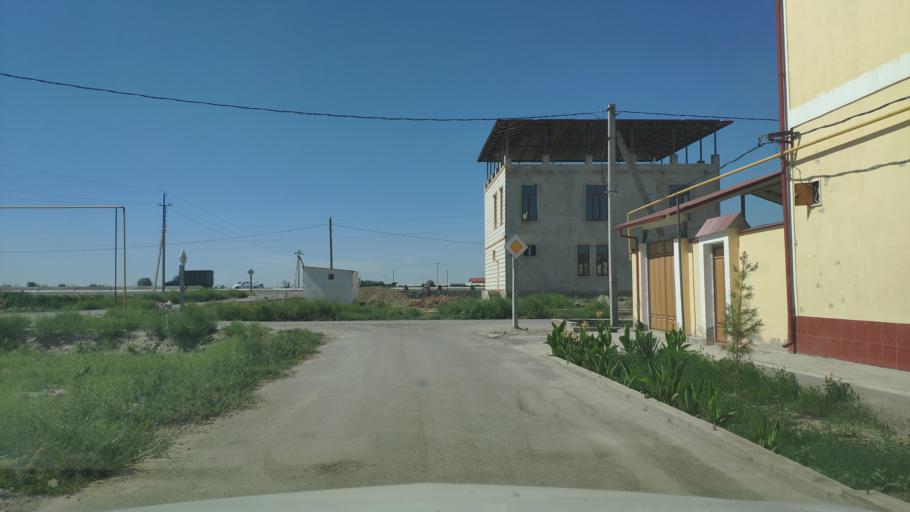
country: UZ
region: Bukhara
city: Bukhara
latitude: 39.7700
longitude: 64.3749
